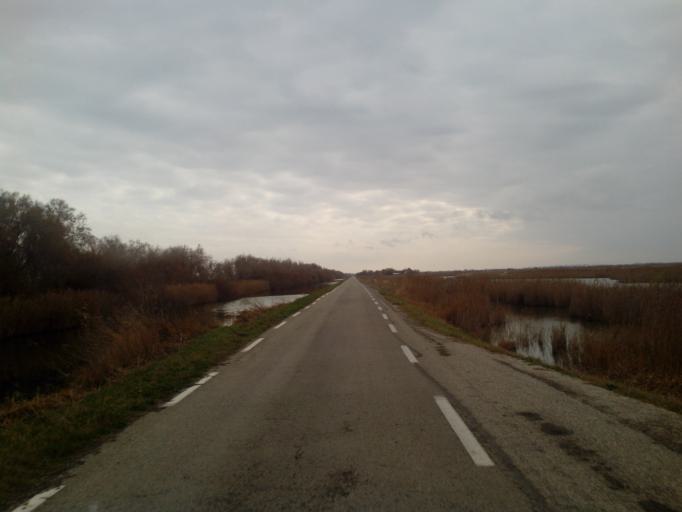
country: FR
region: Languedoc-Roussillon
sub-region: Departement du Gard
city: Vauvert
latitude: 43.6264
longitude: 4.3119
